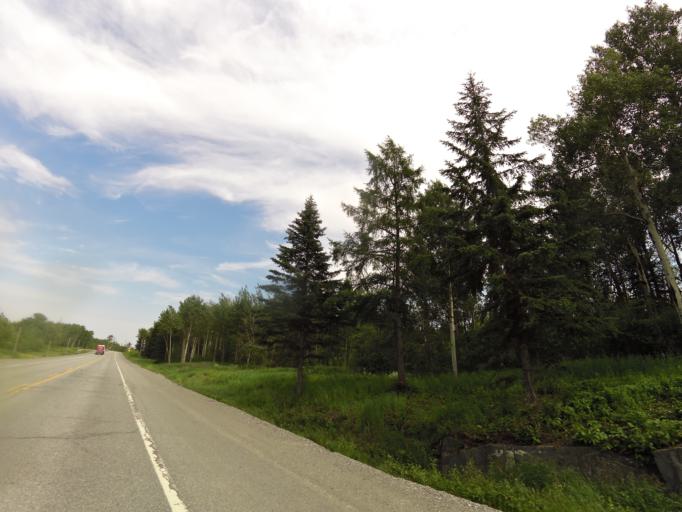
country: CA
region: Quebec
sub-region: Abitibi-Temiscamingue
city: Malartic
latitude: 48.2335
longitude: -78.4178
